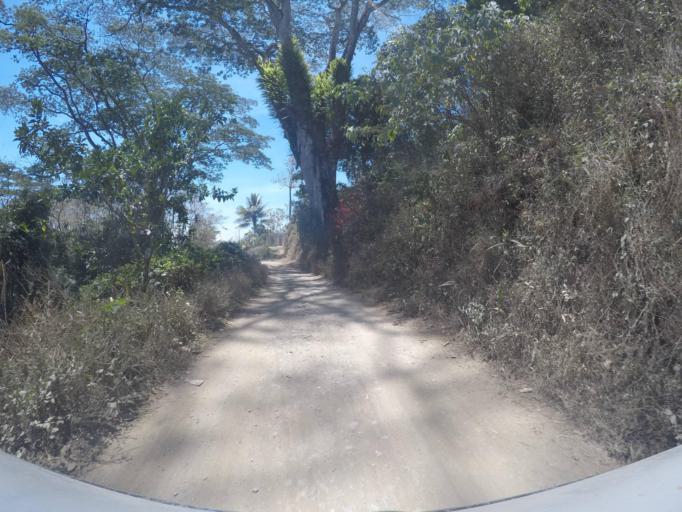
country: TL
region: Ermera
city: Gleno
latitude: -8.7359
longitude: 125.4098
